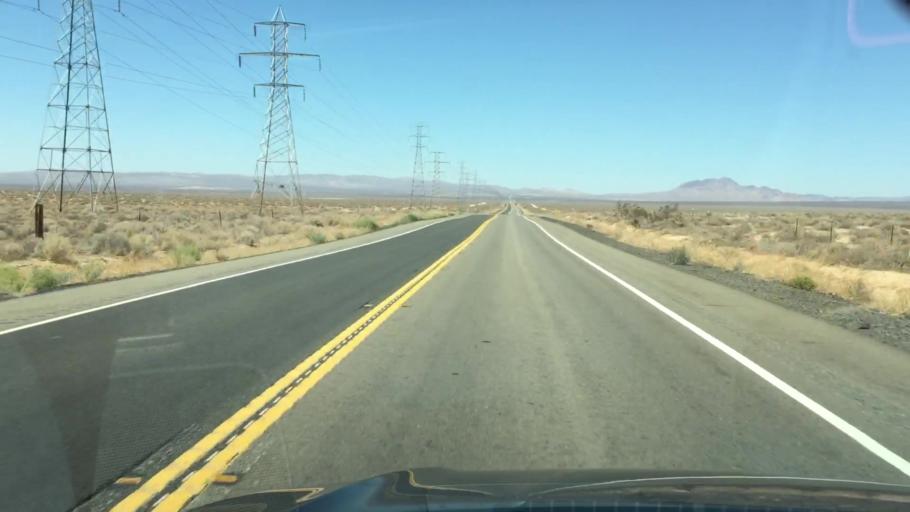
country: US
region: California
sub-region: Kern County
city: Boron
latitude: 35.1368
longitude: -117.5819
